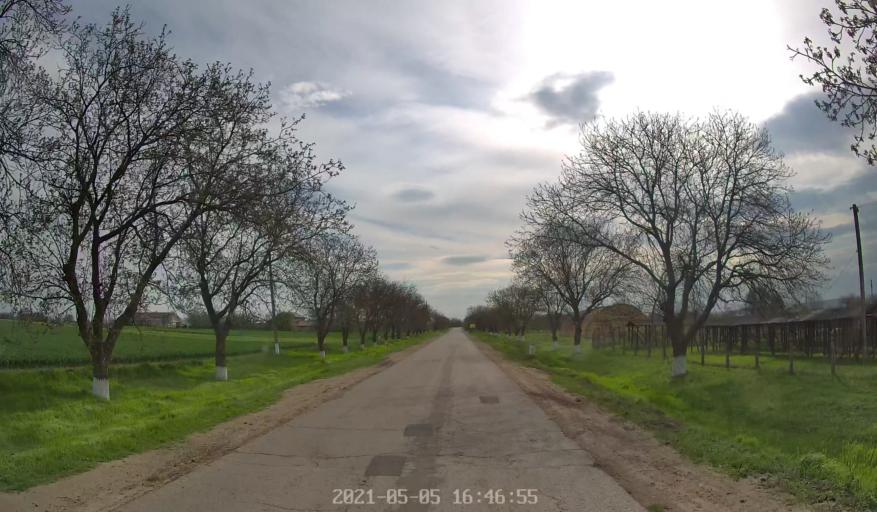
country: MD
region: Chisinau
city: Vadul lui Voda
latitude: 47.0970
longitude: 29.1854
